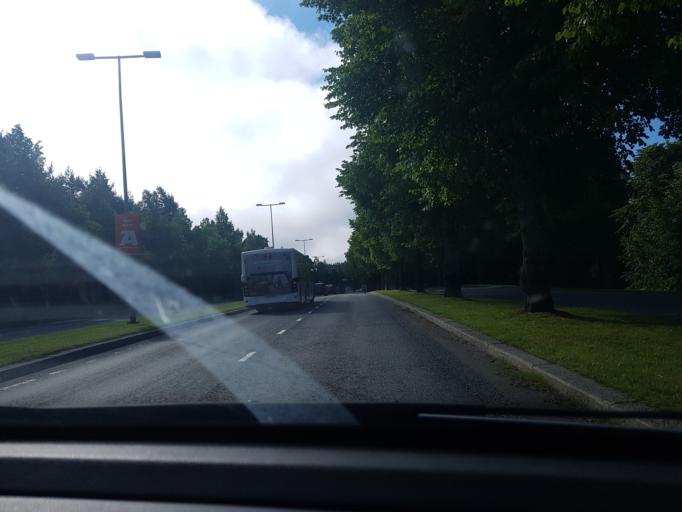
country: FI
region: Northern Savo
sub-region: Kuopio
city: Kuopio
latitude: 62.8982
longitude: 27.6659
